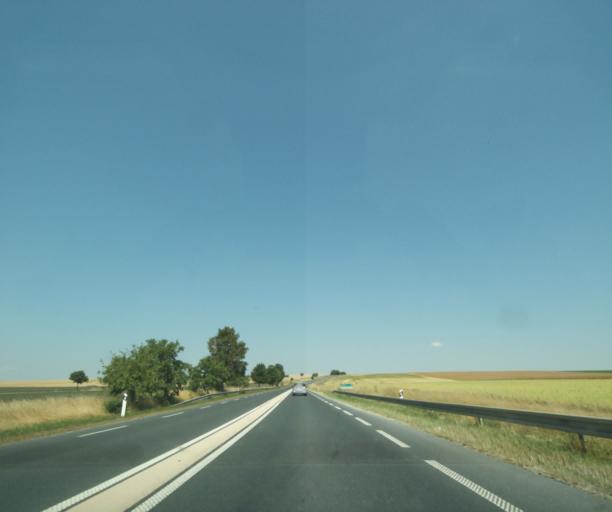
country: FR
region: Champagne-Ardenne
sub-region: Departement de la Marne
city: Mourmelon-le-Grand
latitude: 49.0706
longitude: 4.2931
